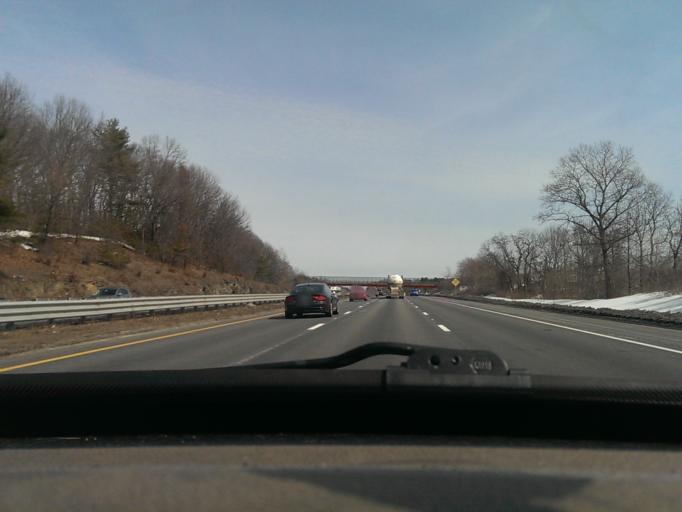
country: US
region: Massachusetts
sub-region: Worcester County
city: Auburn
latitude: 42.2020
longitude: -71.8277
